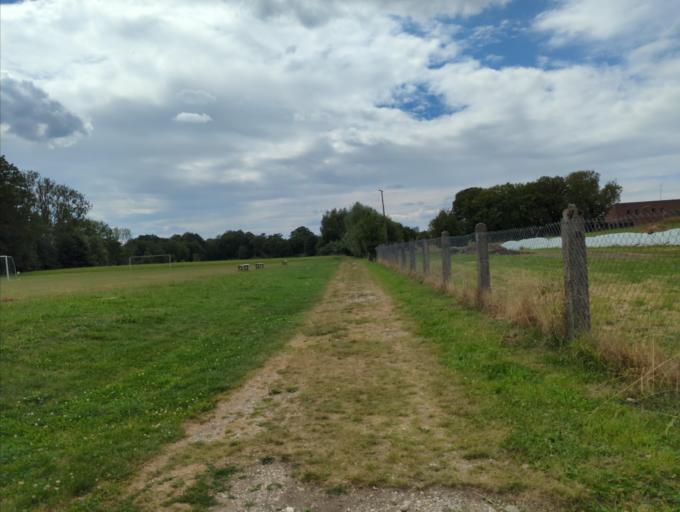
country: DE
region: Bavaria
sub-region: Upper Bavaria
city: Wasserburg am Inn
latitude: 48.0557
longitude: 12.2040
